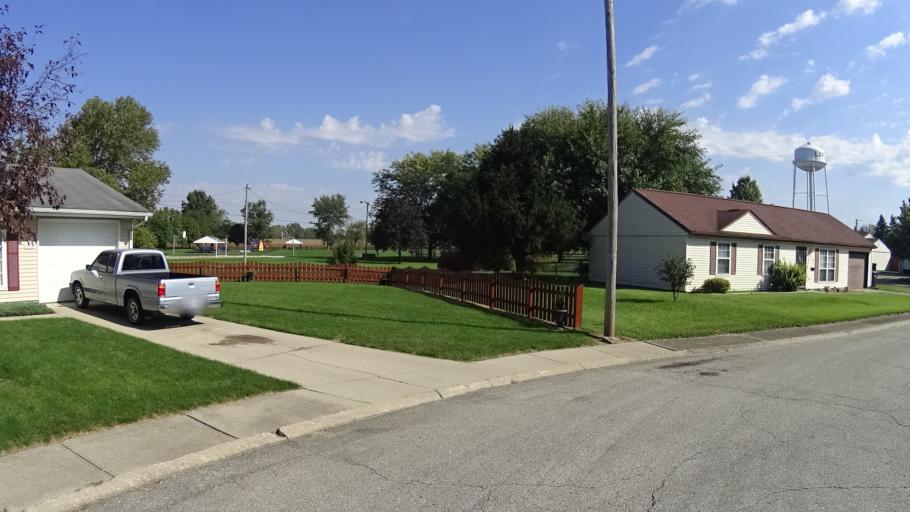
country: US
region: Indiana
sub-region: Madison County
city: Lapel
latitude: 40.0730
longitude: -85.8456
